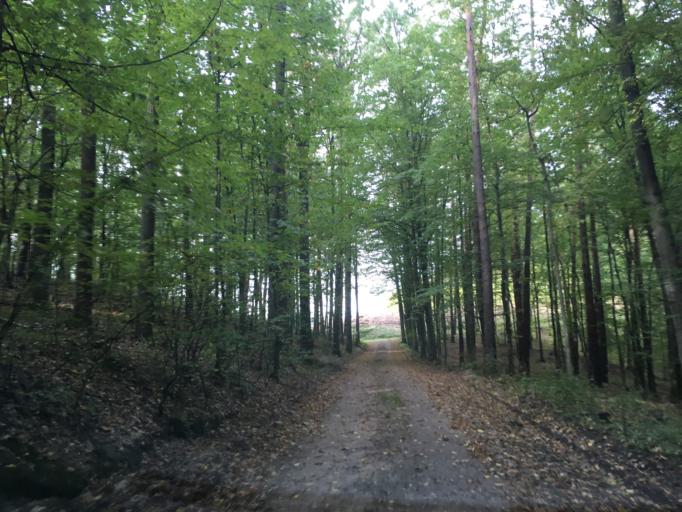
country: PL
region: Kujawsko-Pomorskie
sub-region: Powiat brodnicki
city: Gorzno
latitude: 53.2246
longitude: 19.7051
